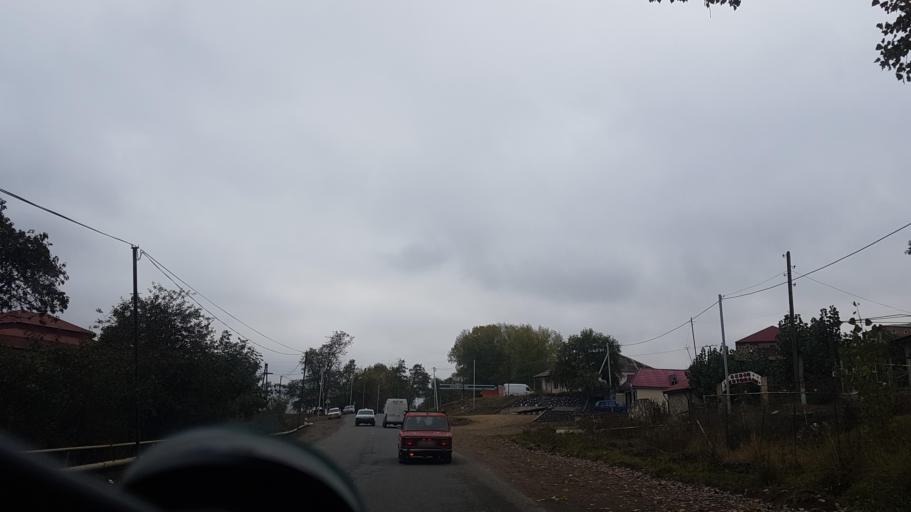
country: AZ
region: Gadabay Rayon
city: Ariqdam
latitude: 40.6525
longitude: 45.8075
